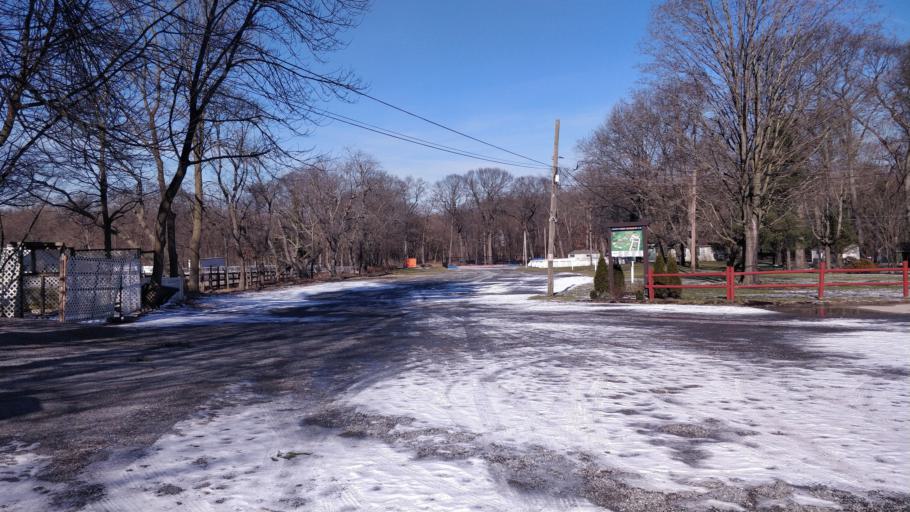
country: US
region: New York
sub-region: Nassau County
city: Brookville
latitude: 40.8135
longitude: -73.5848
